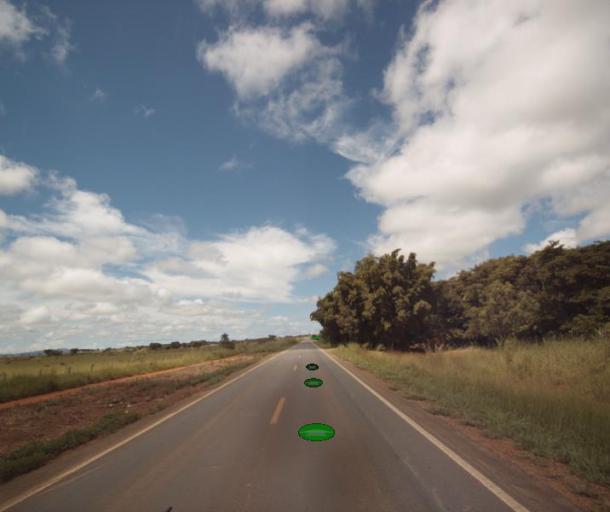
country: BR
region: Goias
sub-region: Padre Bernardo
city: Padre Bernardo
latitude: -15.2376
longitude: -48.2735
